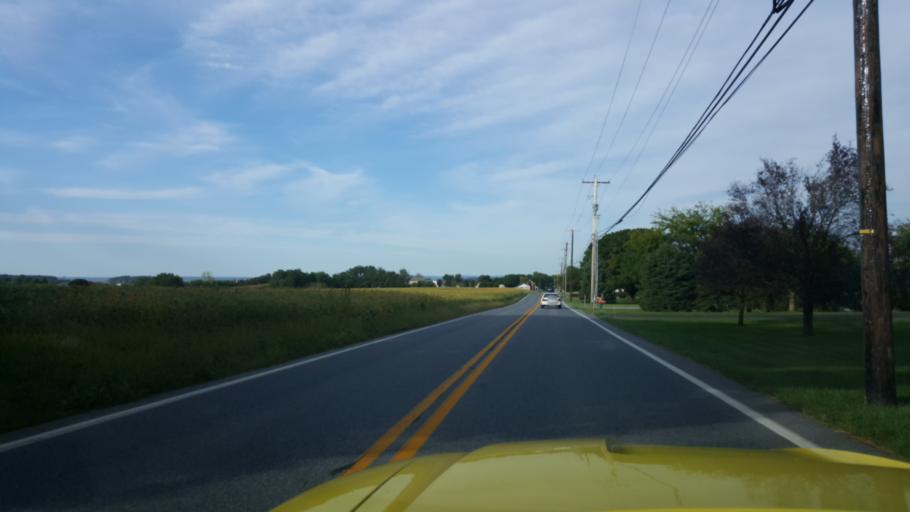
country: US
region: Pennsylvania
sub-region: Lebanon County
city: Campbelltown
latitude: 40.2933
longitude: -76.5679
